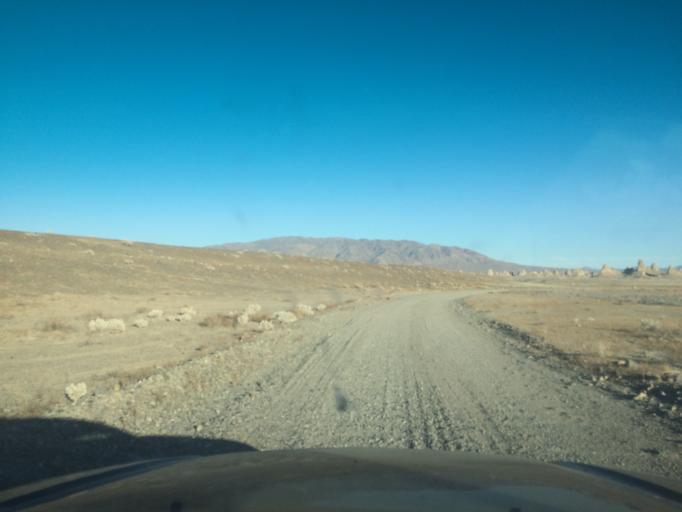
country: US
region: California
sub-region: San Bernardino County
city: Searles Valley
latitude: 35.6246
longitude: -117.3778
